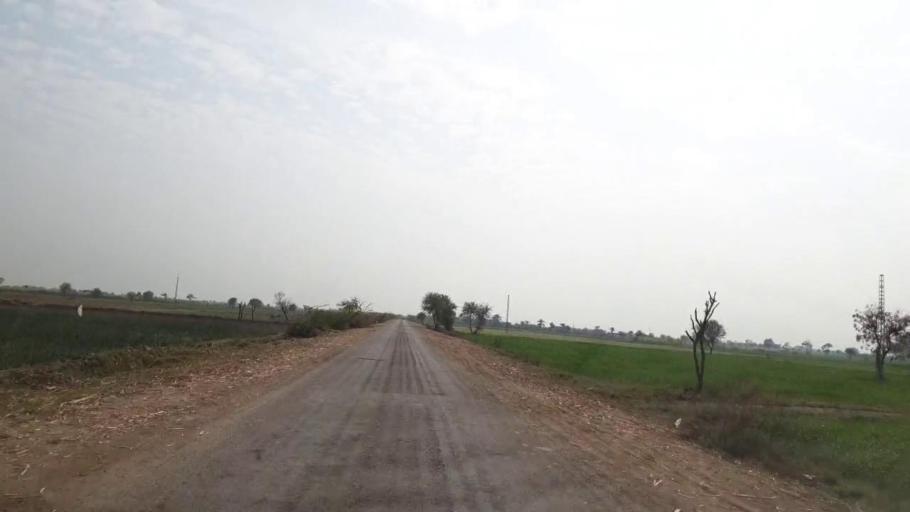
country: PK
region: Sindh
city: Mirpur Khas
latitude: 25.5347
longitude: 69.1570
